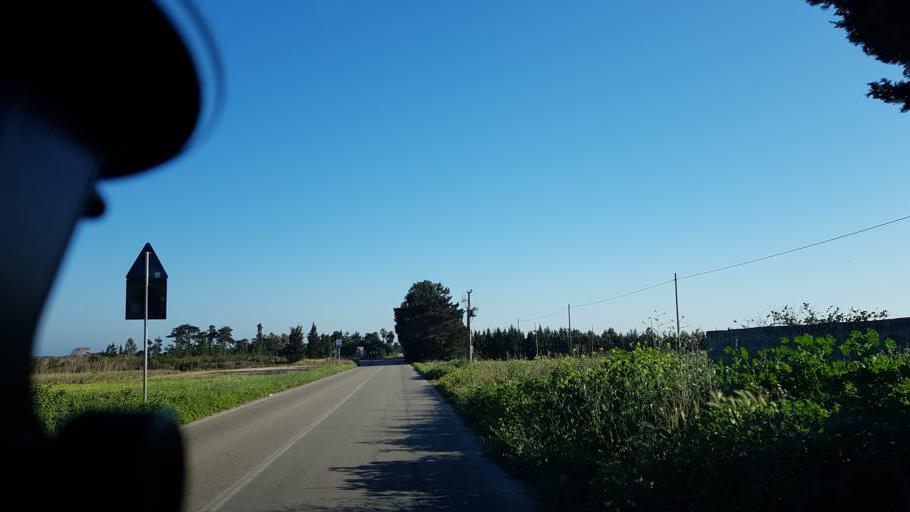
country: IT
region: Apulia
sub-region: Provincia di Lecce
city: Giorgilorio
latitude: 40.4447
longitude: 18.2310
